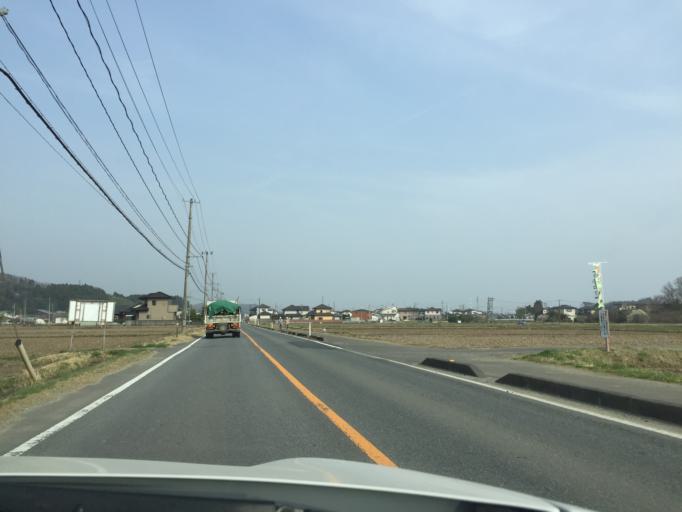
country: JP
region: Fukushima
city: Iwaki
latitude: 36.9596
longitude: 140.8351
